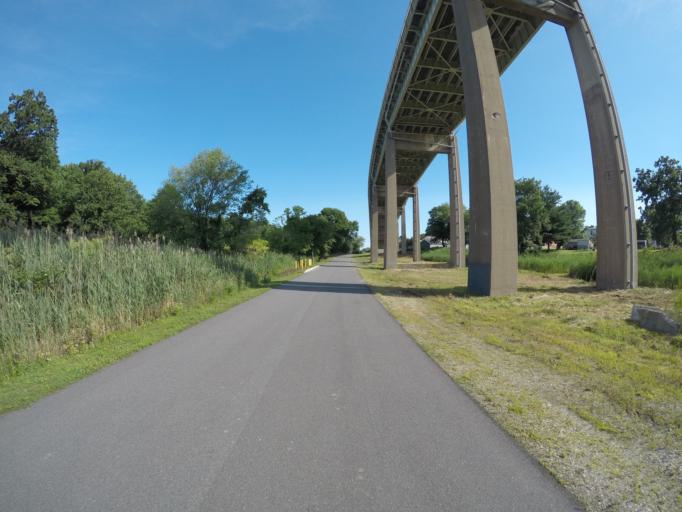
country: US
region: Delaware
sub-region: New Castle County
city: Delaware City
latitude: 39.5545
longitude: -75.6524
